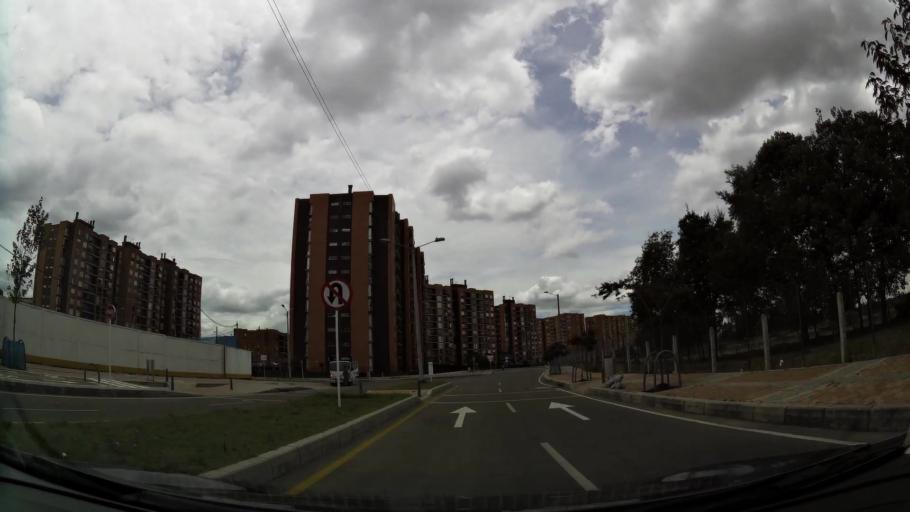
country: CO
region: Cundinamarca
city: Funza
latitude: 4.7244
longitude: -74.1266
